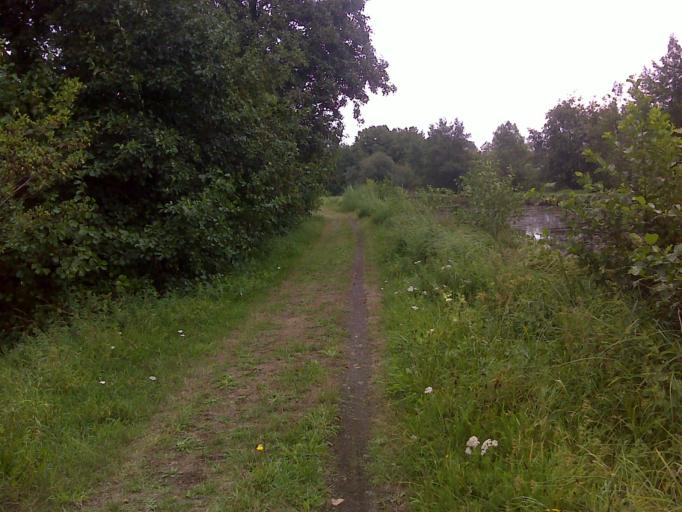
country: FR
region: Nord-Pas-de-Calais
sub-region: Departement du Nord
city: Landrecies
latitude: 50.1111
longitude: 3.6612
